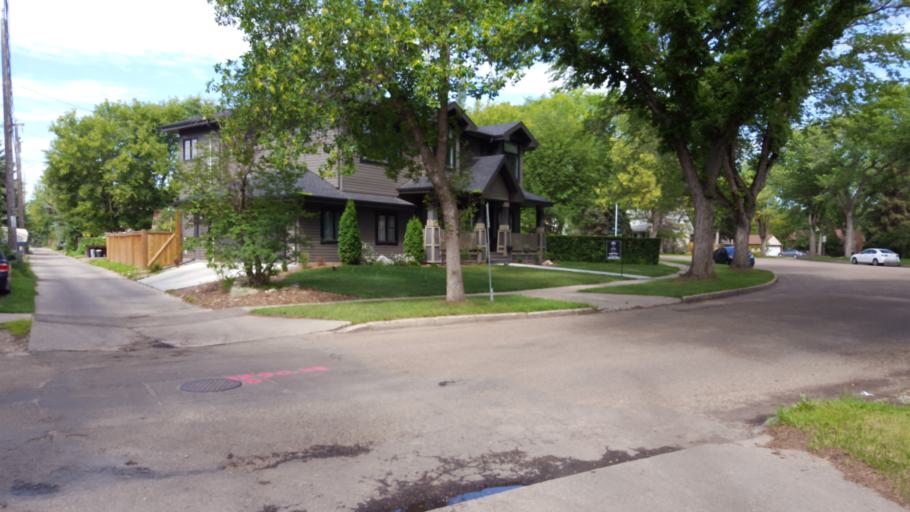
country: CA
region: Alberta
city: Edmonton
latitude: 53.5128
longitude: -113.5312
